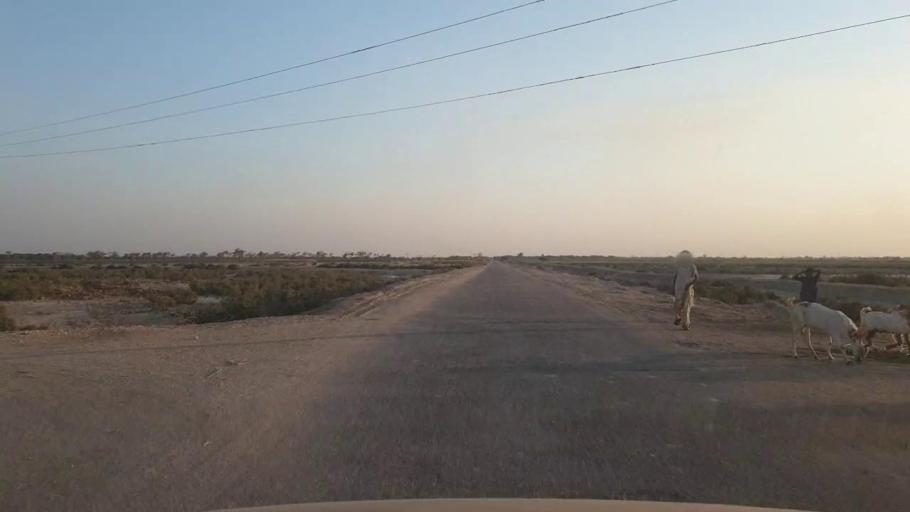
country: PK
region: Sindh
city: Mirwah Gorchani
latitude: 25.2781
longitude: 68.9395
